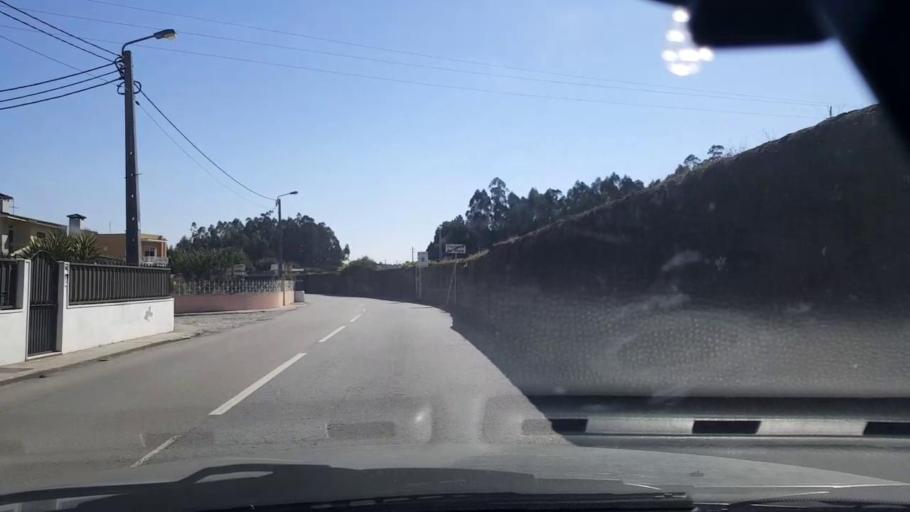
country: PT
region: Porto
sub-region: Vila do Conde
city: Arvore
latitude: 41.3349
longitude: -8.6822
